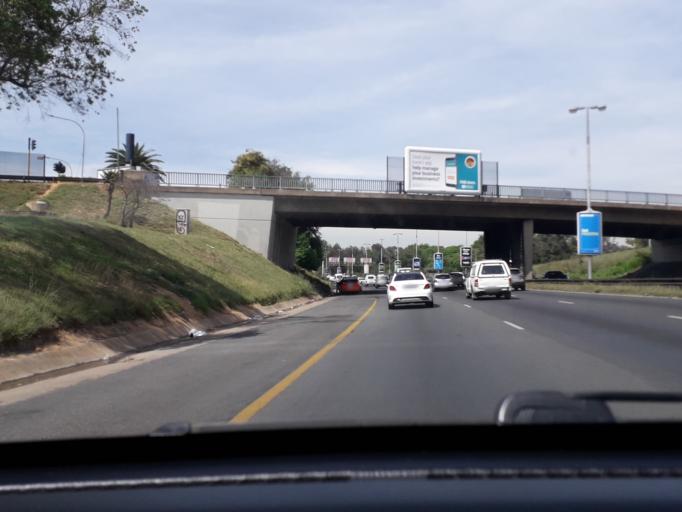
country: ZA
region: Gauteng
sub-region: City of Johannesburg Metropolitan Municipality
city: Johannesburg
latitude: -26.1459
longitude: 28.0587
